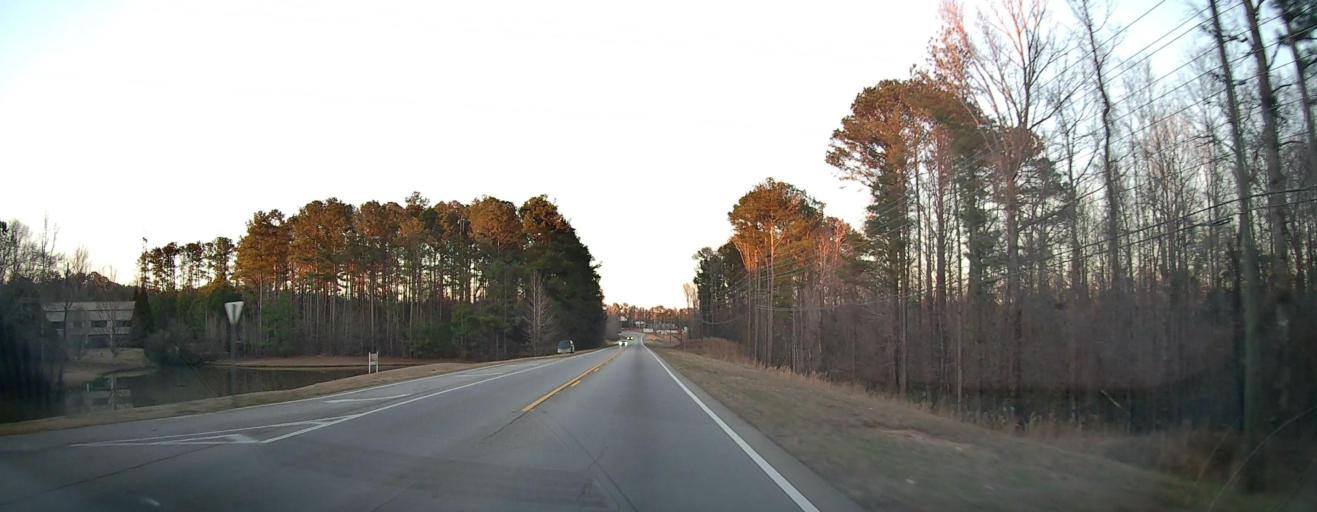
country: US
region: Georgia
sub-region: Troup County
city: La Grange
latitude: 33.0254
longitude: -84.9913
